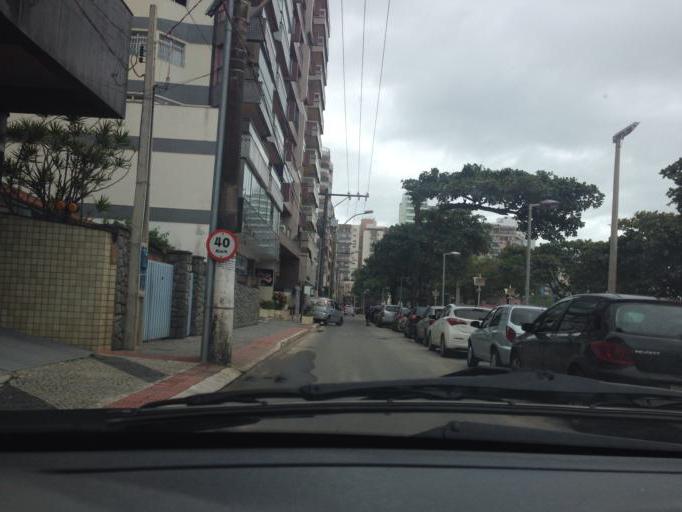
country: BR
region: Espirito Santo
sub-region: Guarapari
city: Guarapari
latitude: -20.6733
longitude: -40.4977
